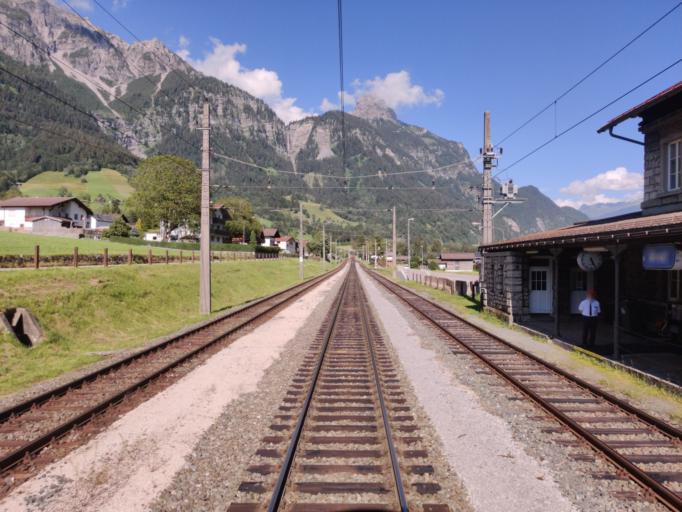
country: AT
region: Vorarlberg
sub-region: Politischer Bezirk Bludenz
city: Innerbraz
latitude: 47.1477
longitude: 9.8948
